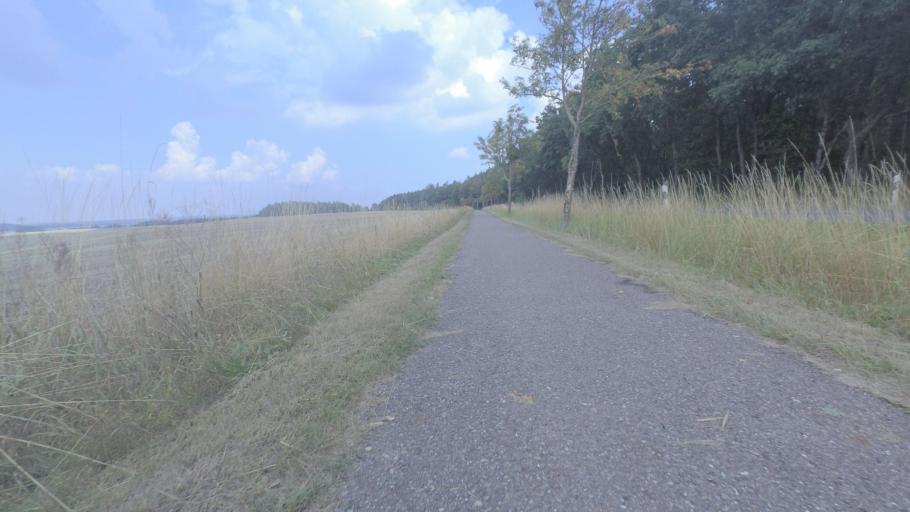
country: DE
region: Mecklenburg-Vorpommern
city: Malchin
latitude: 53.7505
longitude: 12.8327
